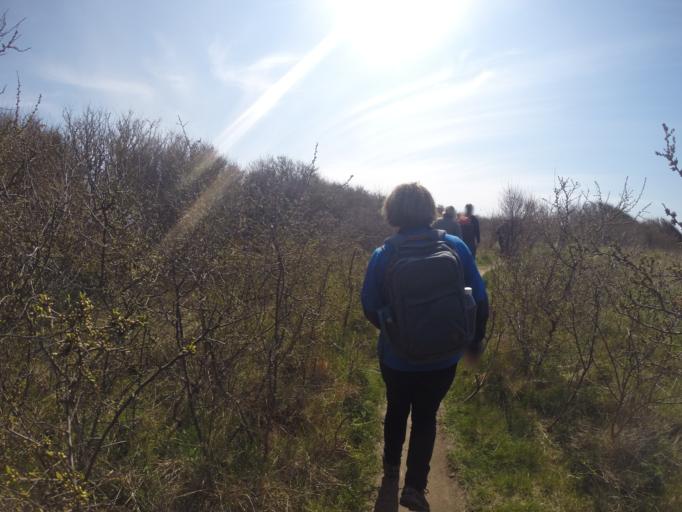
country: DK
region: Zealand
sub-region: Kalundborg Kommune
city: Gorlev
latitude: 55.5255
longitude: 11.0855
